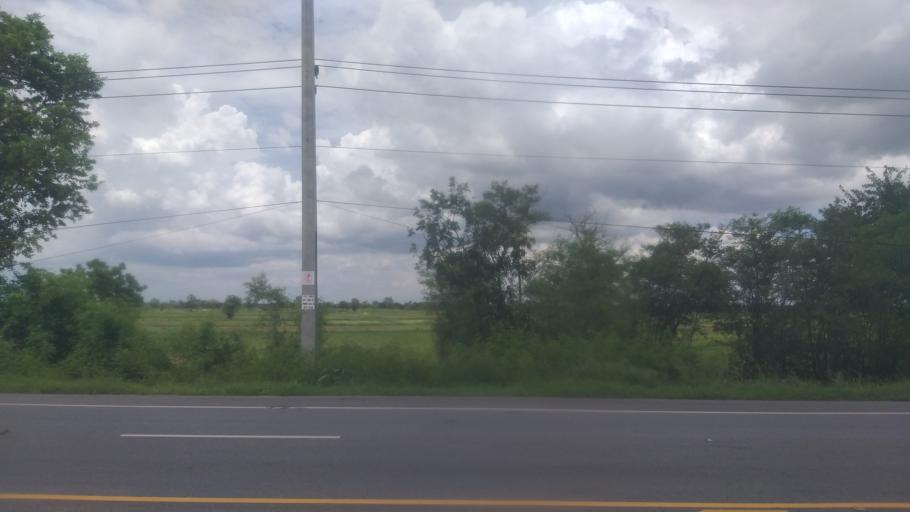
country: TH
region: Nakhon Ratchasima
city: Non Thai
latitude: 15.1207
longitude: 102.1025
